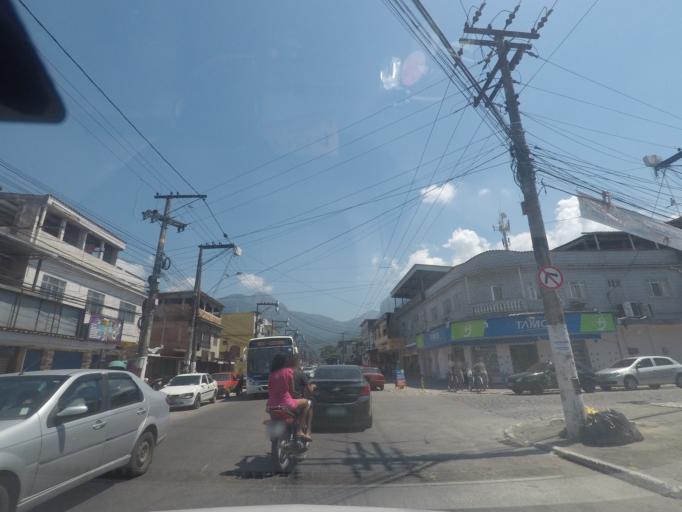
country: BR
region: Rio de Janeiro
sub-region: Petropolis
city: Petropolis
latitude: -22.5913
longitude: -43.1866
